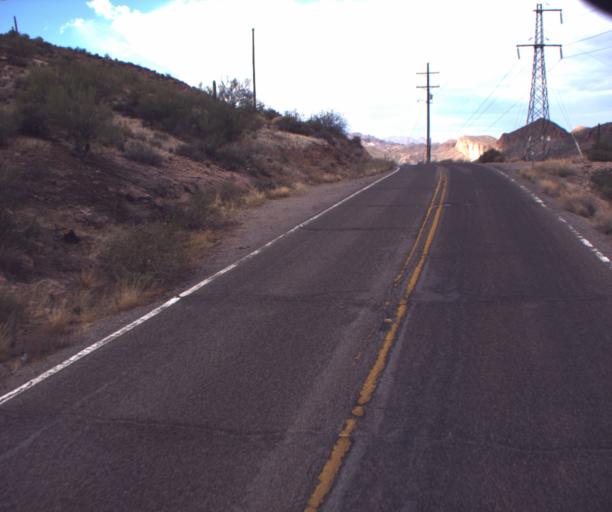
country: US
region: Arizona
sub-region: Pinal County
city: Apache Junction
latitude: 33.5291
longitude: -111.4020
